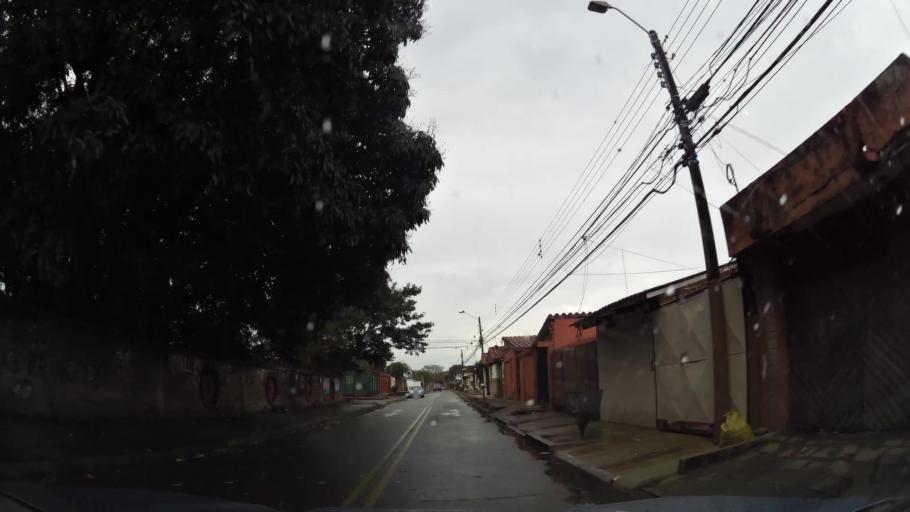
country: BO
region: Santa Cruz
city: Santa Cruz de la Sierra
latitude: -17.7708
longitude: -63.1534
